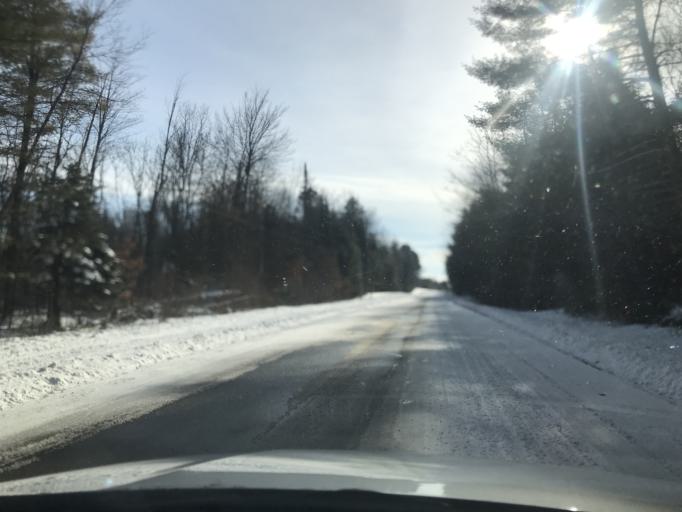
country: US
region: Wisconsin
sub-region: Oconto County
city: Gillett
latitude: 45.1353
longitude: -88.2497
